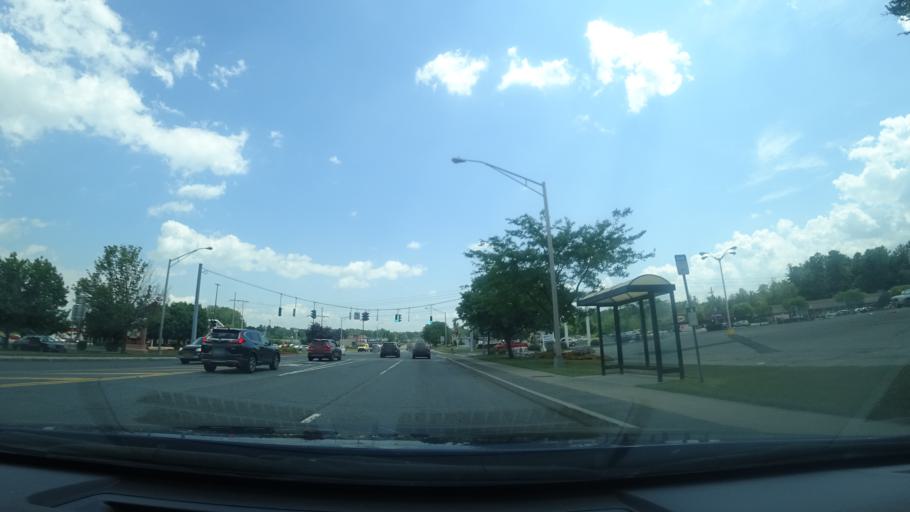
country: US
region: New York
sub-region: Warren County
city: Glens Falls North
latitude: 43.3295
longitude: -73.6717
